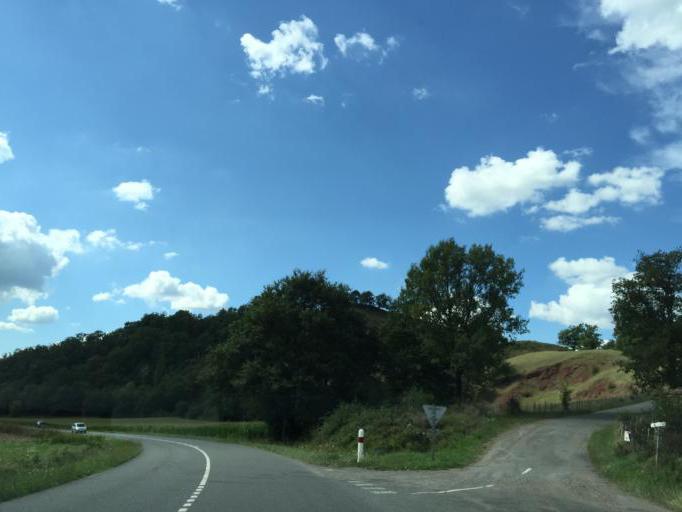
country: FR
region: Midi-Pyrenees
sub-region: Departement de l'Aveyron
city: Saint-Christophe-Vallon
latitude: 44.5244
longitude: 2.4231
